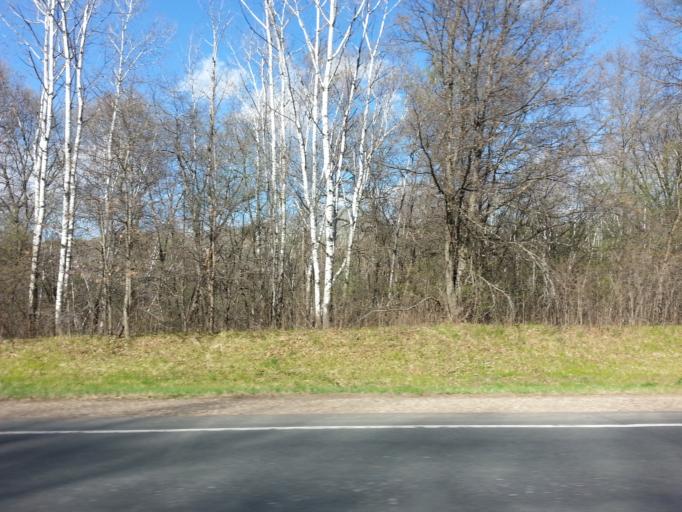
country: US
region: Wisconsin
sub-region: Saint Croix County
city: North Hudson
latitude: 45.0374
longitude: -92.6838
